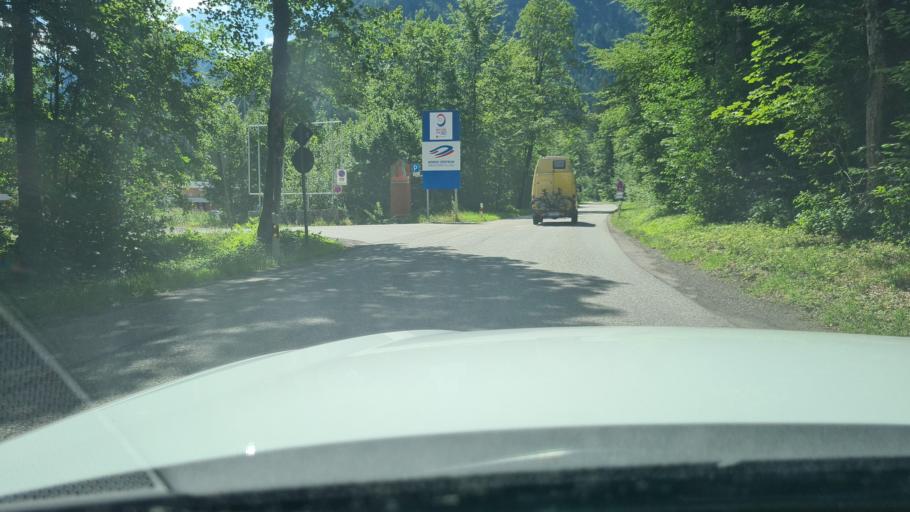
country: DE
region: Bavaria
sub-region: Swabia
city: Oberstdorf
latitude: 47.3852
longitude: 10.2810
